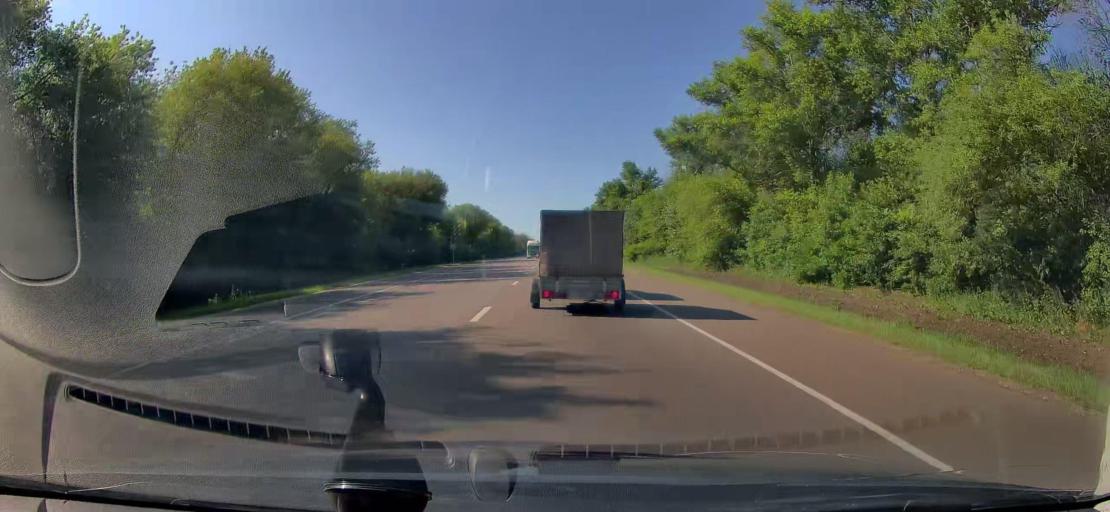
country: RU
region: Orjol
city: Kromy
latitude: 52.6098
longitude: 35.7626
